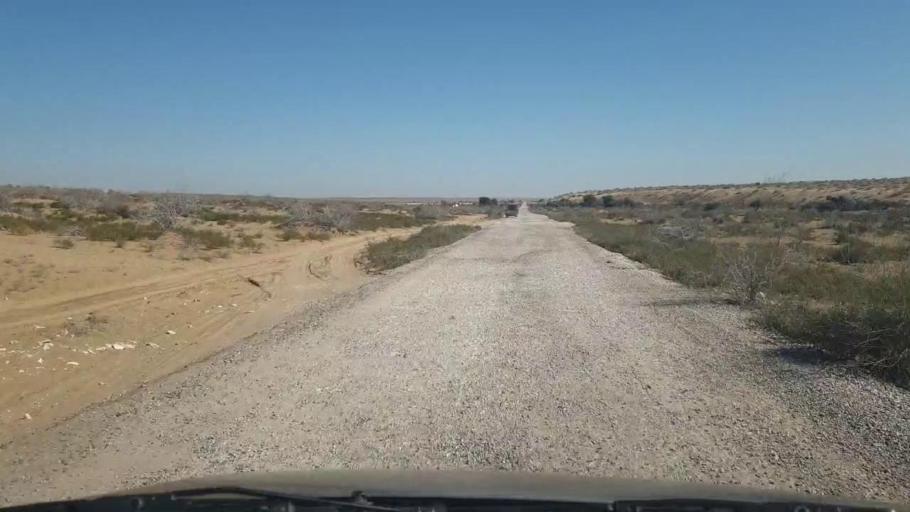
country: PK
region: Sindh
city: Bozdar
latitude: 27.0135
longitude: 68.7400
